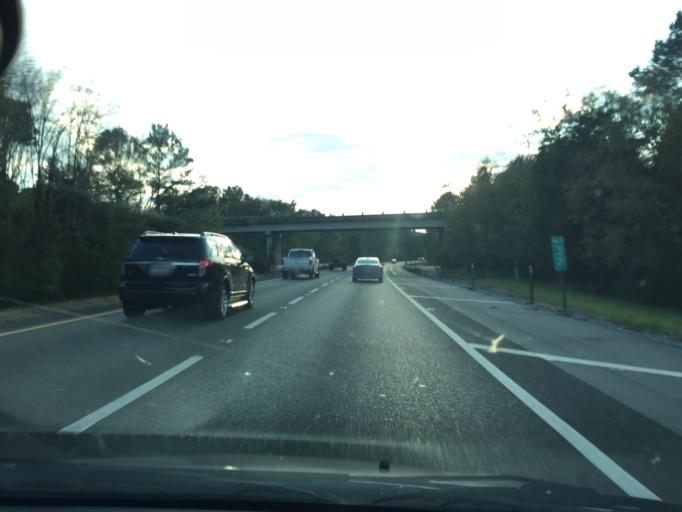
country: US
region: Tennessee
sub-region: Bradley County
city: Hopewell
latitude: 35.3296
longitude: -84.7622
